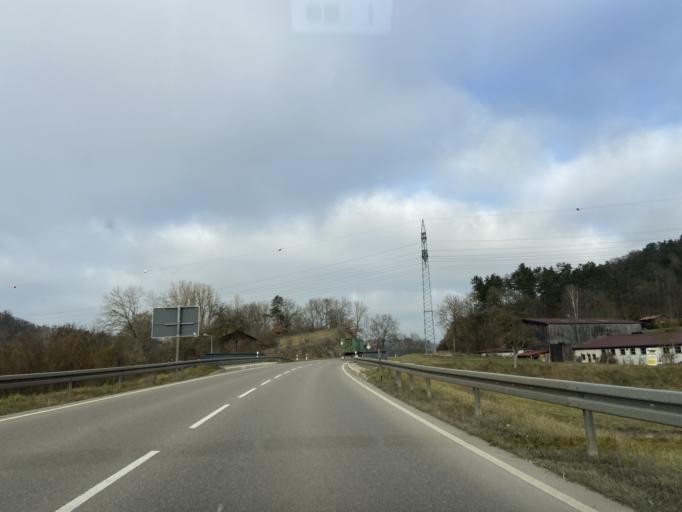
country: DE
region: Baden-Wuerttemberg
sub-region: Tuebingen Region
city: Veringenstadt
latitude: 48.1613
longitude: 9.2000
